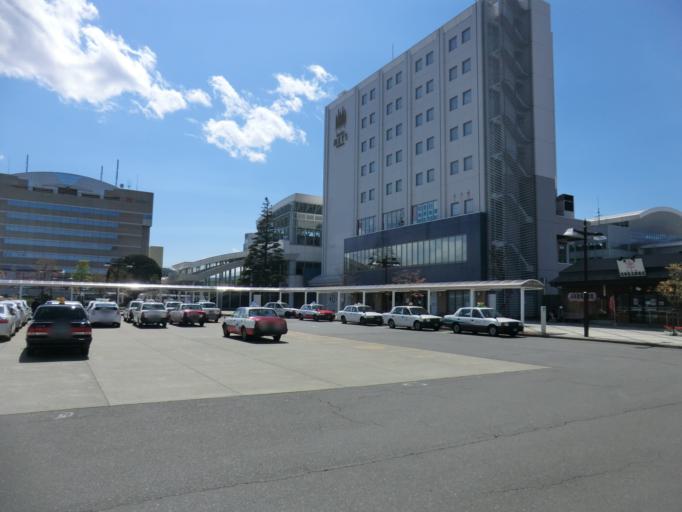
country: JP
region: Aomori
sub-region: Hachinohe Shi
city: Uchimaru
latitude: 40.5093
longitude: 141.4332
